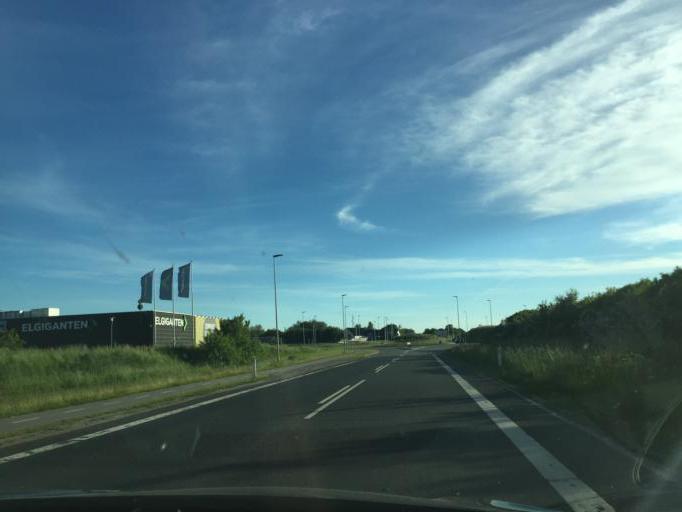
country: DK
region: Zealand
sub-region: Slagelse Kommune
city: Slagelse
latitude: 55.3890
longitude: 11.3241
